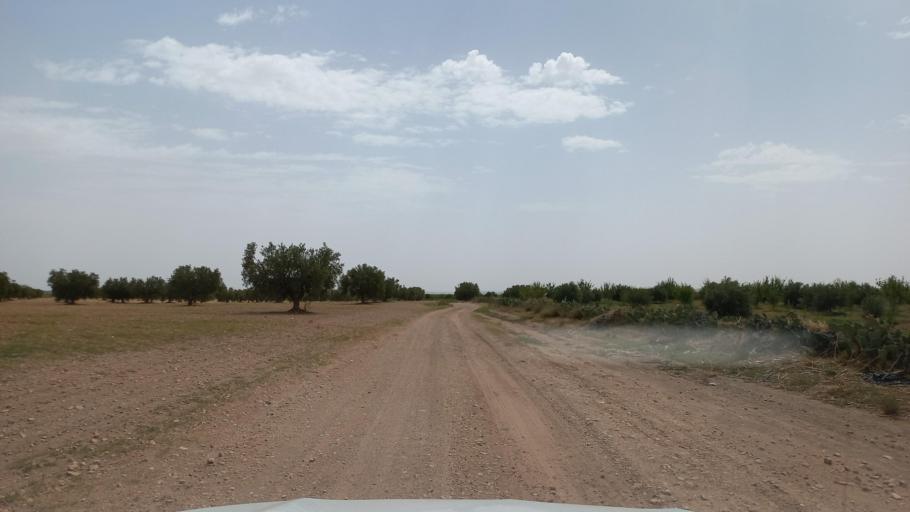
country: TN
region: Al Qasrayn
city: Kasserine
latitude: 35.2926
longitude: 9.0196
